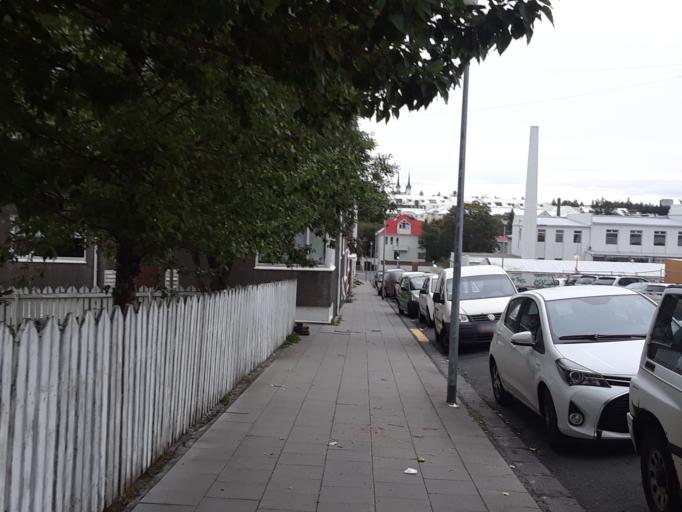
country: IS
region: Capital Region
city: Reykjavik
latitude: 64.1421
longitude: -21.9204
